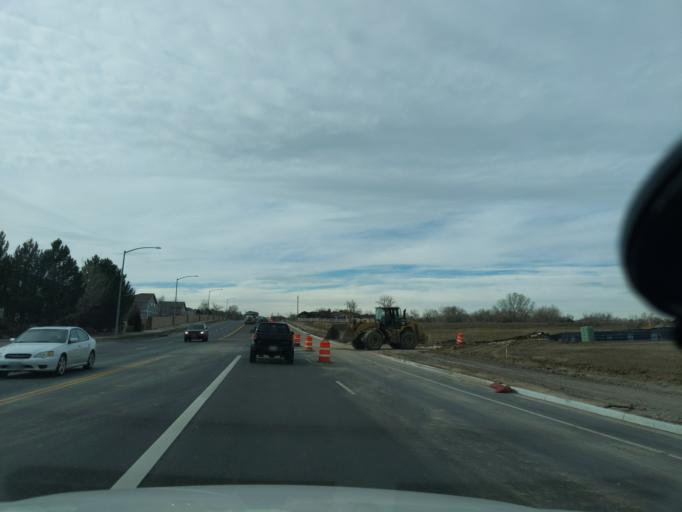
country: US
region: Colorado
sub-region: Adams County
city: Thornton
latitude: 39.8995
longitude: -104.9511
